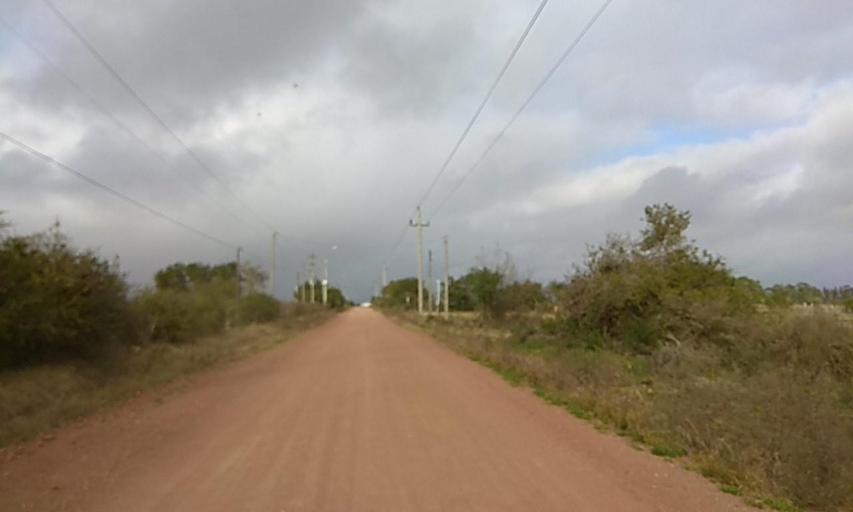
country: UY
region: Florida
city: Florida
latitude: -34.0605
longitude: -56.2164
